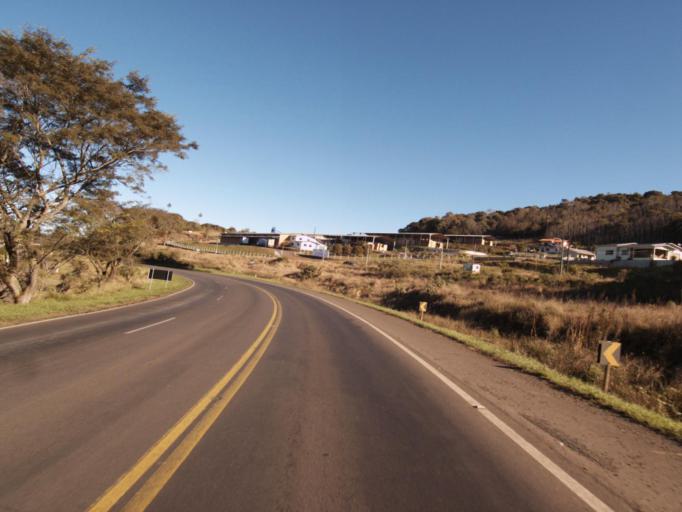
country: BR
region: Santa Catarina
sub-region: Chapeco
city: Chapeco
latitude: -26.9875
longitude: -52.6108
